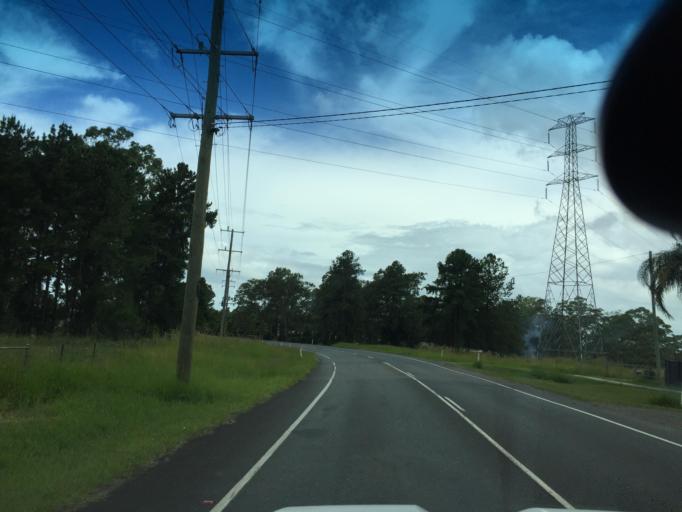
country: AU
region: Queensland
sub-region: Moreton Bay
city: Caboolture
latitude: -27.0679
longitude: 152.9148
